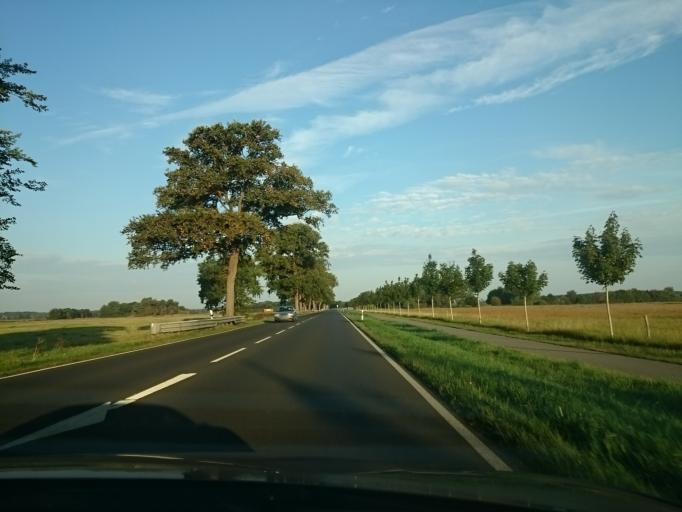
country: DE
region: Mecklenburg-Vorpommern
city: Ostseebad Zinnowitz
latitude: 54.0694
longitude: 13.8867
